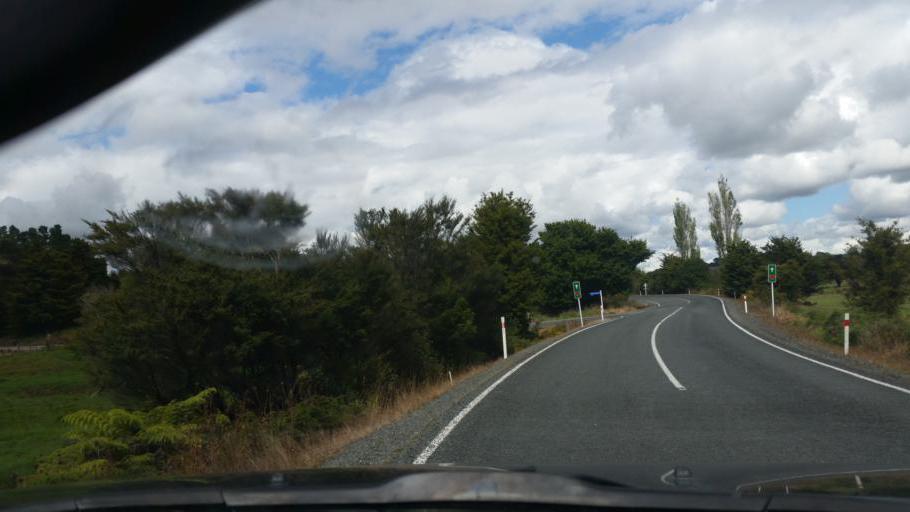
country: NZ
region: Northland
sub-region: Whangarei
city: Ruakaka
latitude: -35.9420
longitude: 174.2927
